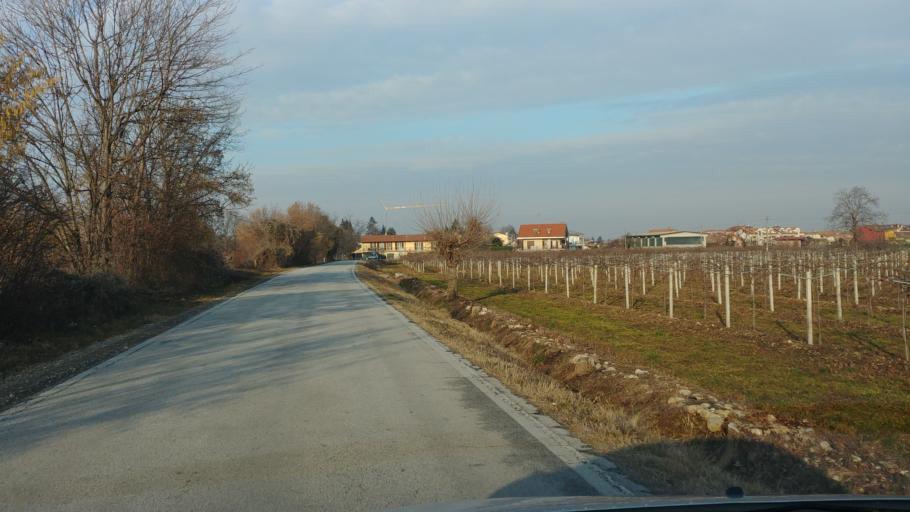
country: IT
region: Piedmont
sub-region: Provincia di Cuneo
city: Cuneo
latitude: 44.4081
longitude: 7.5400
